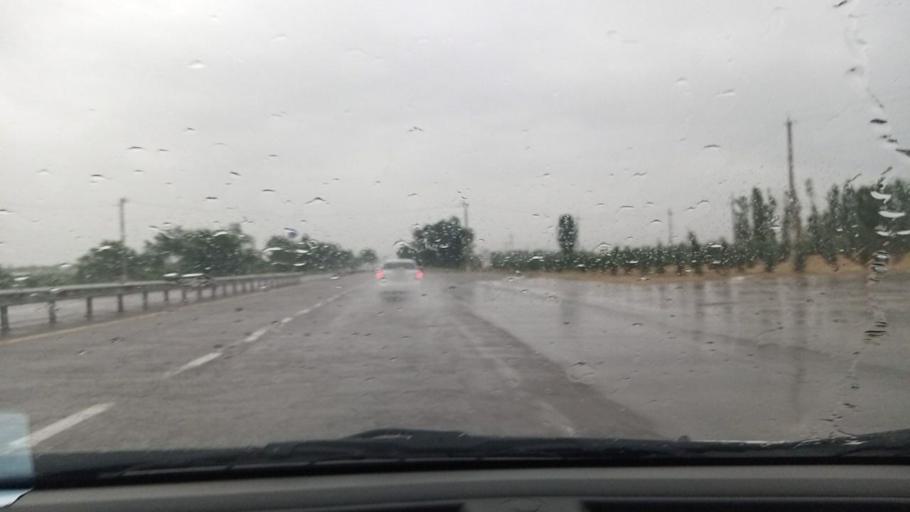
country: UZ
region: Toshkent
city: Ohangaron
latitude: 40.9390
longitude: 69.5841
